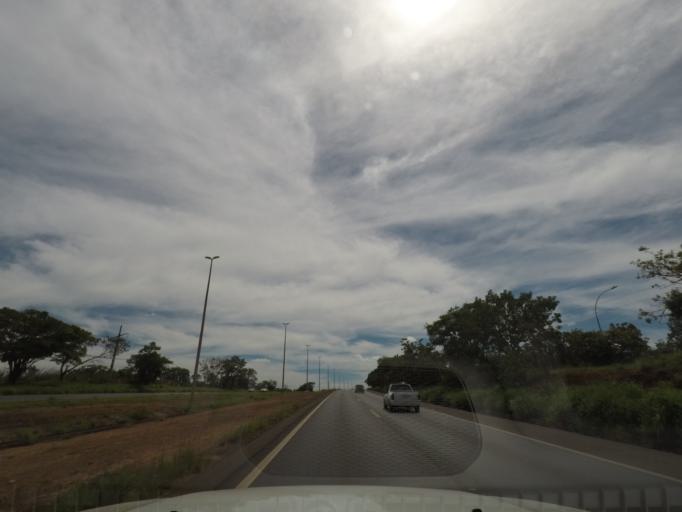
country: BR
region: Goias
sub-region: Planaltina
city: Planaltina
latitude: -15.5947
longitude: -47.6645
